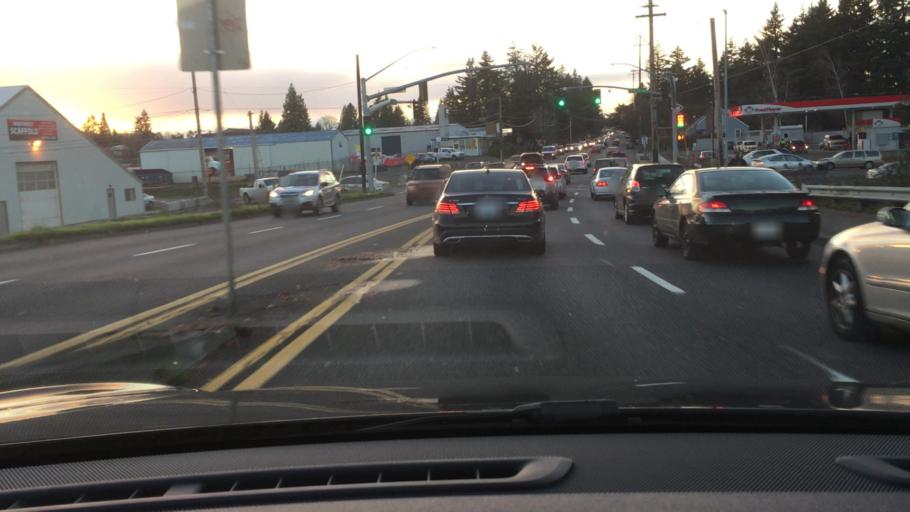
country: US
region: Oregon
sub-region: Multnomah County
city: Lents
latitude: 45.5335
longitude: -122.5677
